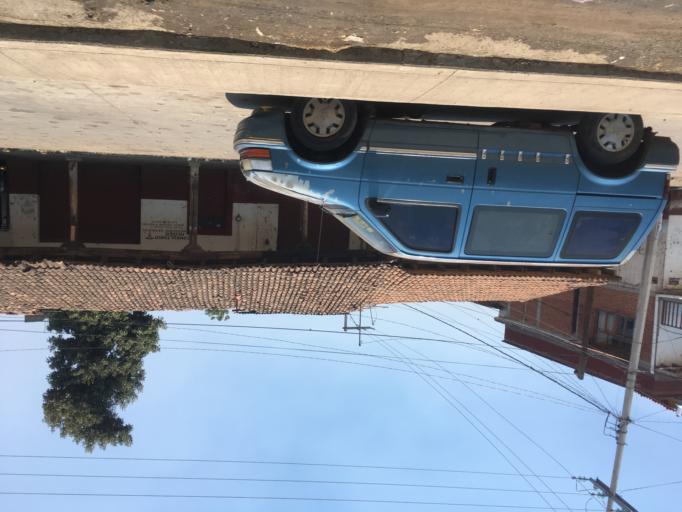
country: MX
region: Michoacan
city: Santa Fe de la Laguna
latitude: 19.6715
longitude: -101.5575
